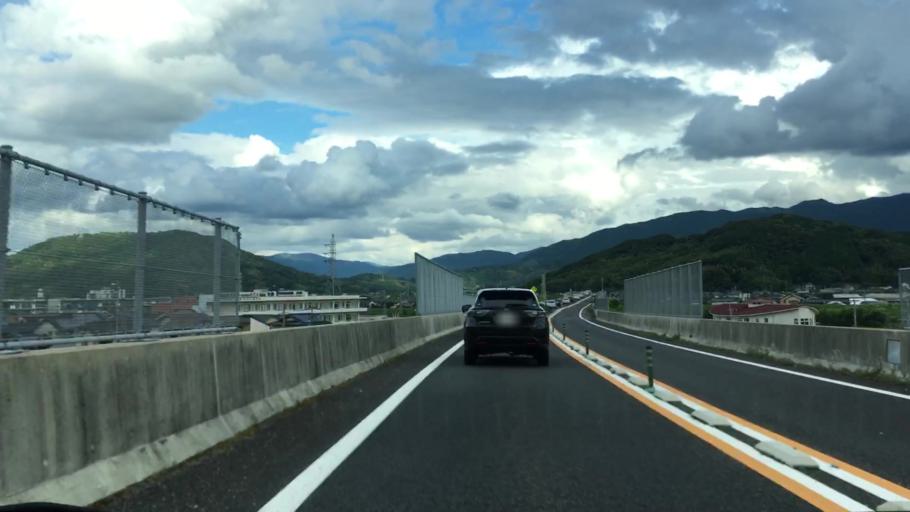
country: JP
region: Saga Prefecture
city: Karatsu
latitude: 33.4120
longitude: 129.9821
